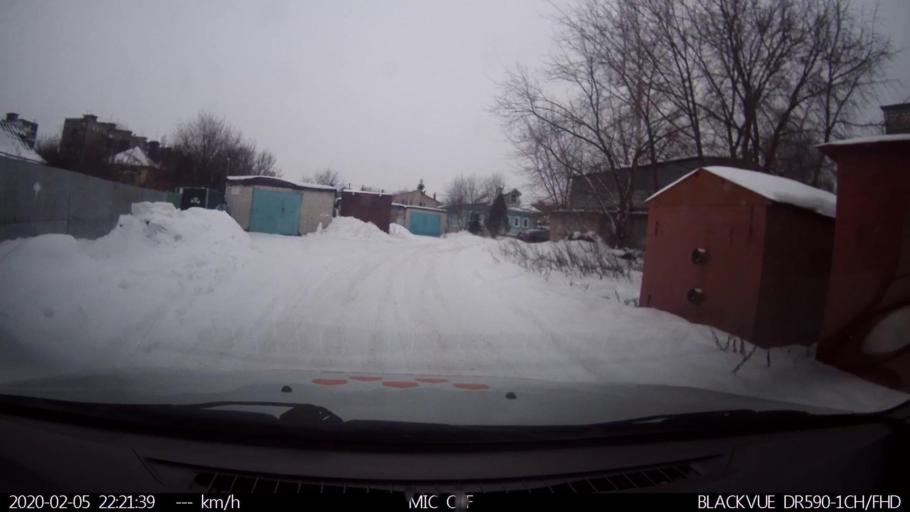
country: RU
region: Nizjnij Novgorod
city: Pervomaysk
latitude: 54.7601
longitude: 43.9972
